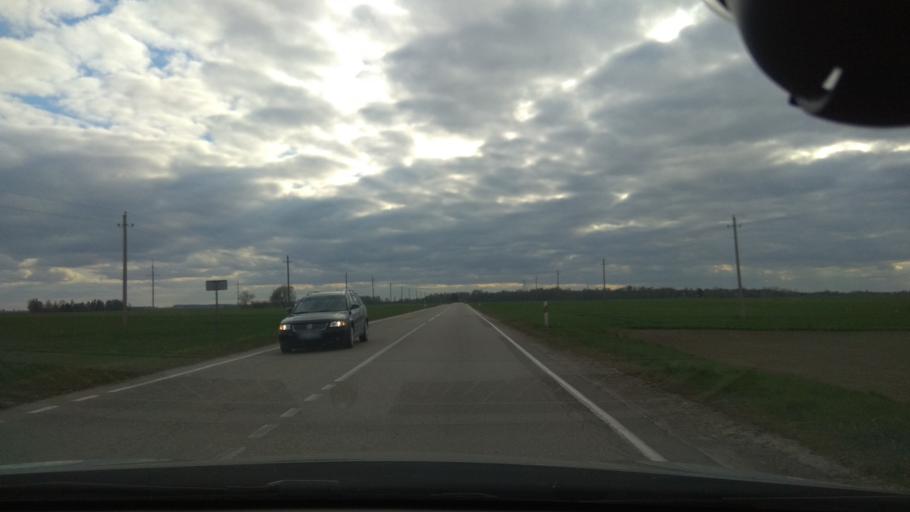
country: LT
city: Linkuva
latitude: 56.1554
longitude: 23.8042
